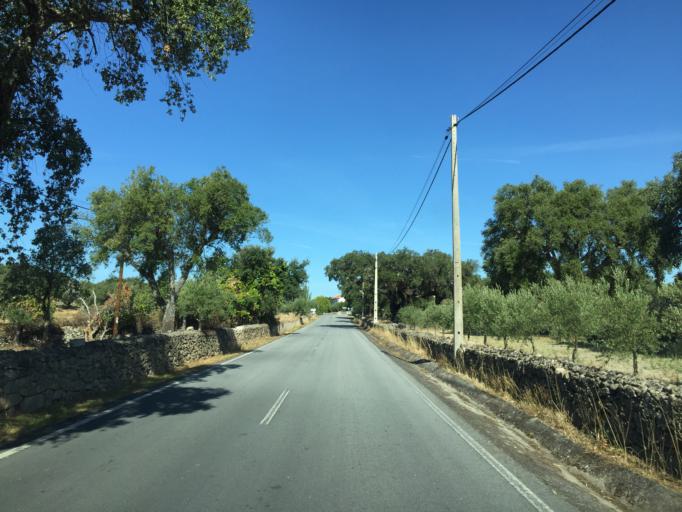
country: PT
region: Portalegre
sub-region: Marvao
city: Marvao
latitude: 39.4299
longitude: -7.3581
